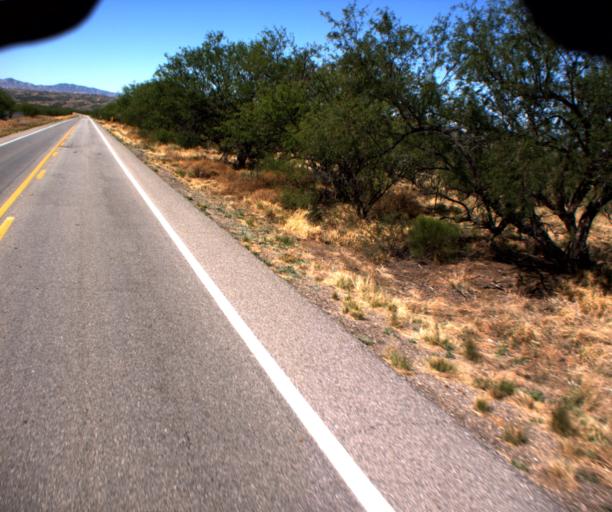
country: US
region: Arizona
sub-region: Santa Cruz County
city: Nogales
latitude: 31.4124
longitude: -110.8577
